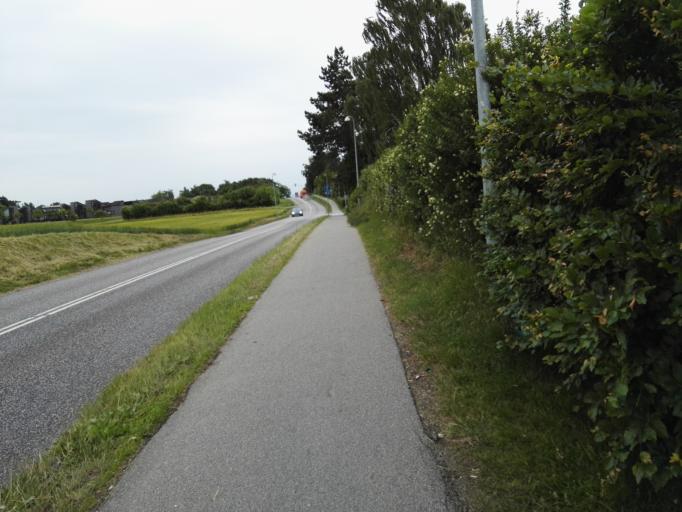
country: DK
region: Zealand
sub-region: Roskilde Kommune
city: Jyllinge
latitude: 55.7630
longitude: 12.1160
